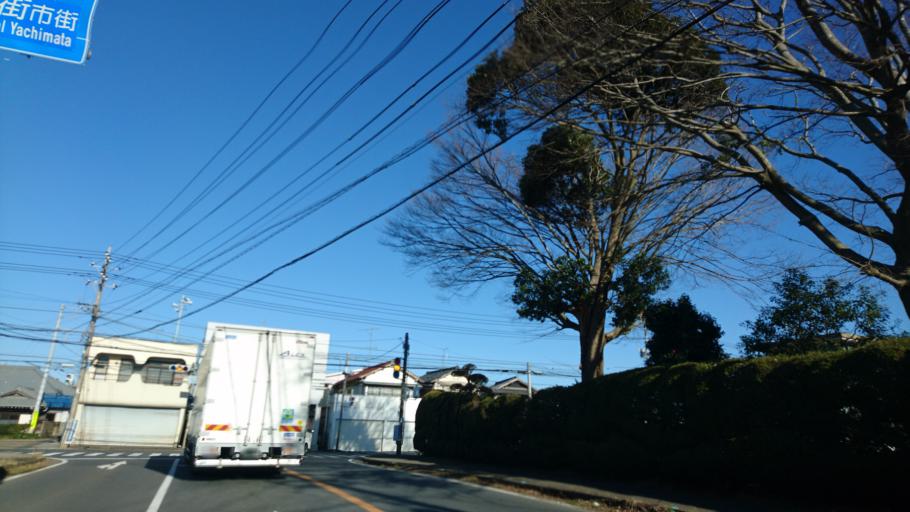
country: JP
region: Chiba
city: Oami
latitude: 35.5745
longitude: 140.2953
